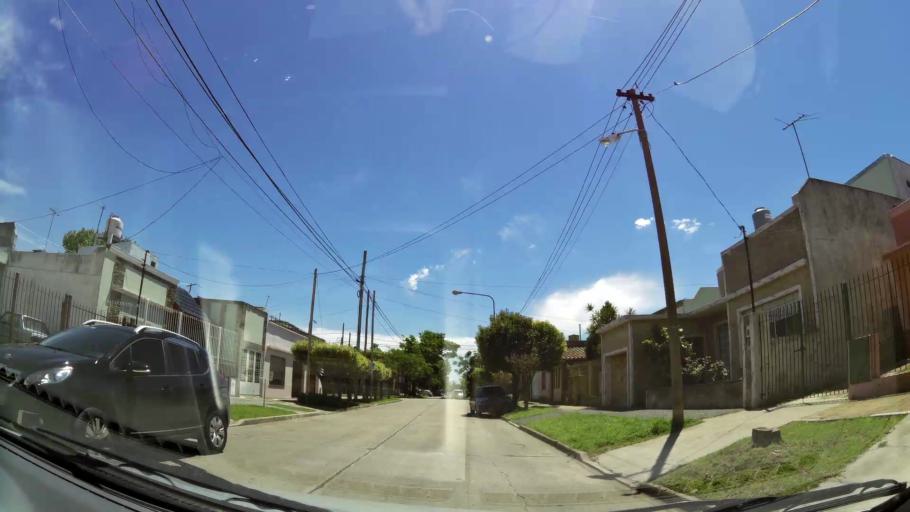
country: AR
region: Buenos Aires
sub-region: Partido de Quilmes
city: Quilmes
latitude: -34.7354
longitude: -58.2911
